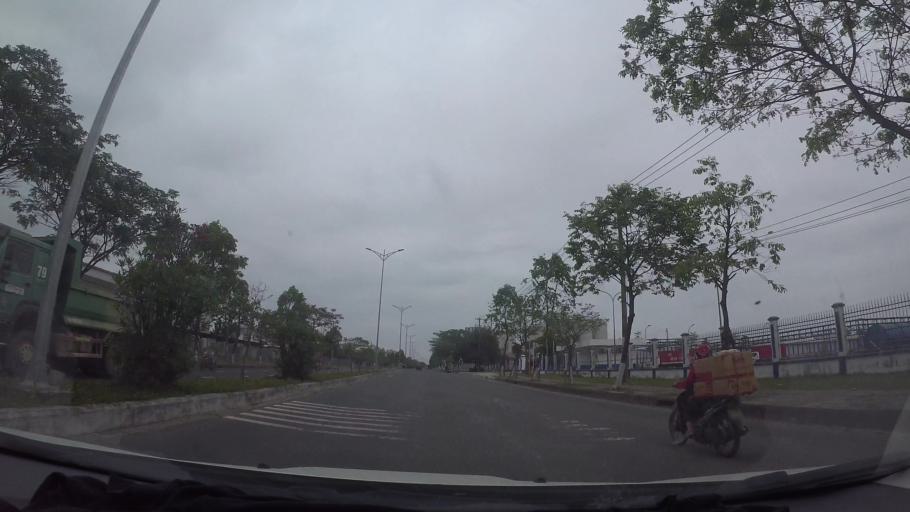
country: VN
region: Da Nang
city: Lien Chieu
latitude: 16.0777
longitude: 108.1403
